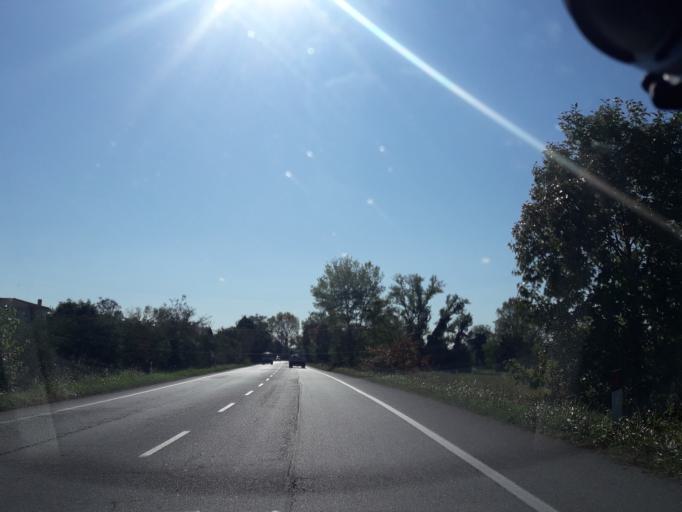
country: IT
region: Friuli Venezia Giulia
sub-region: Provincia di Udine
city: Povoletto
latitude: 46.1104
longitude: 13.2807
